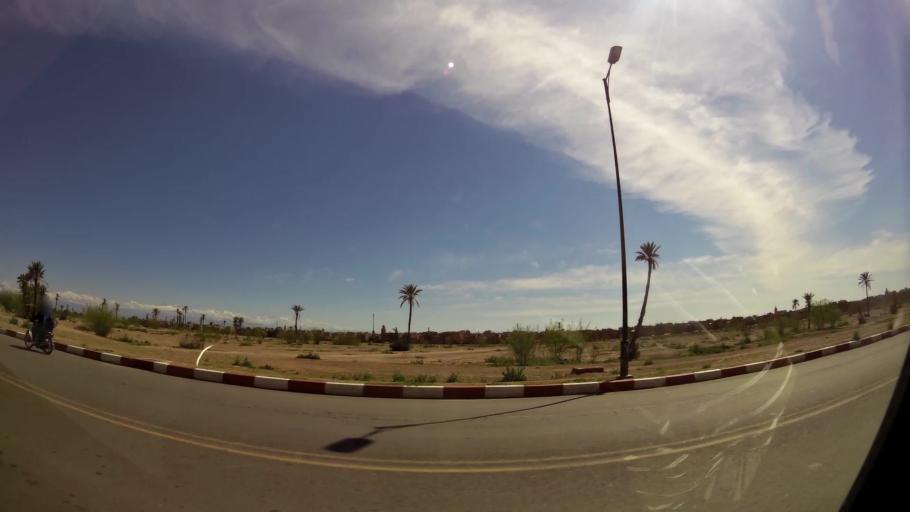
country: MA
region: Marrakech-Tensift-Al Haouz
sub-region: Marrakech
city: Marrakesh
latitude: 31.6197
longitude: -7.9613
